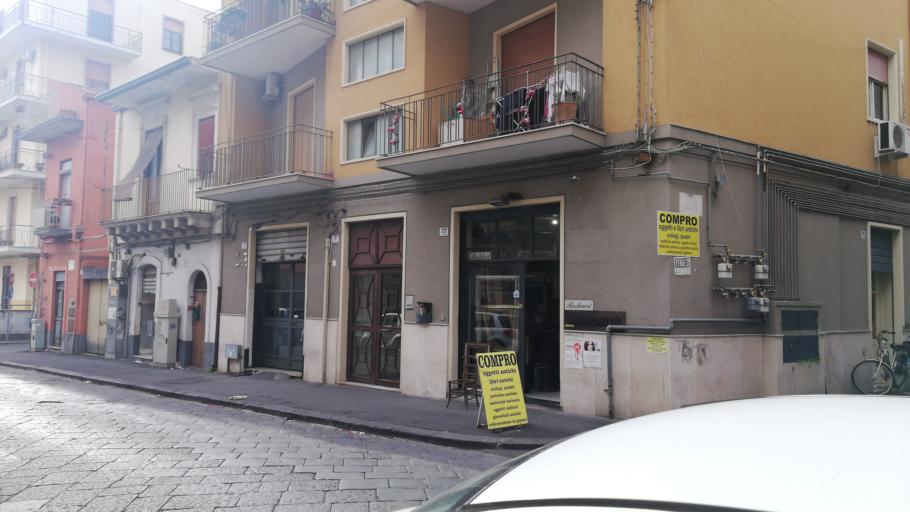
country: IT
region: Sicily
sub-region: Catania
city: Canalicchio
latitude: 37.5192
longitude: 15.0843
